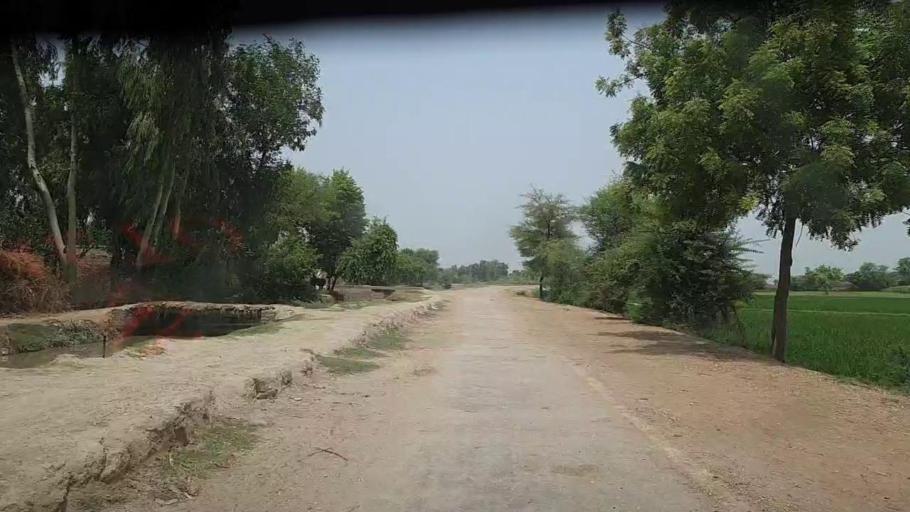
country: PK
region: Sindh
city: Sita Road
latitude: 27.0401
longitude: 67.9022
